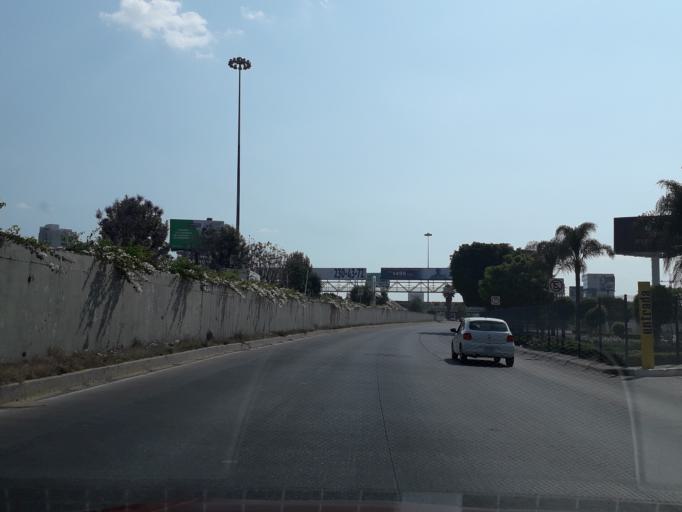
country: MX
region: Puebla
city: Puebla
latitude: 19.0309
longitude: -98.2298
